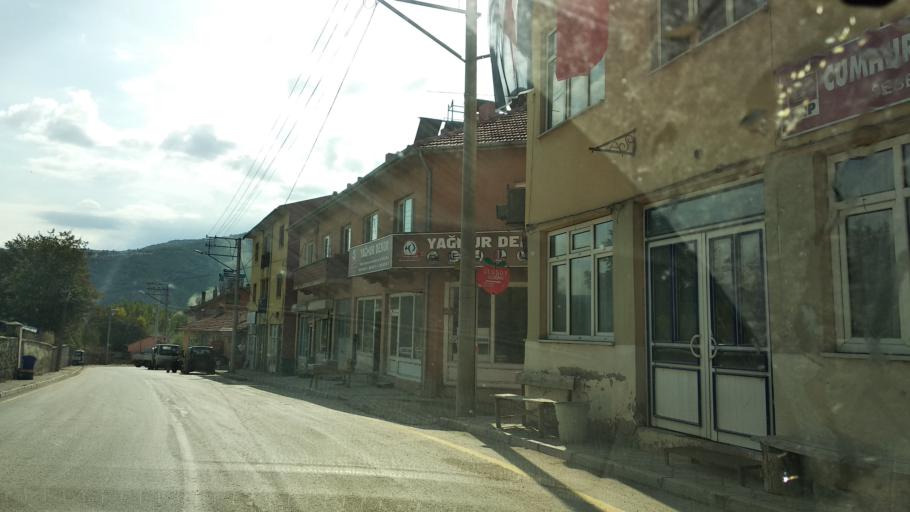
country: TR
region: Bolu
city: Seben
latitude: 40.4082
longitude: 31.5724
